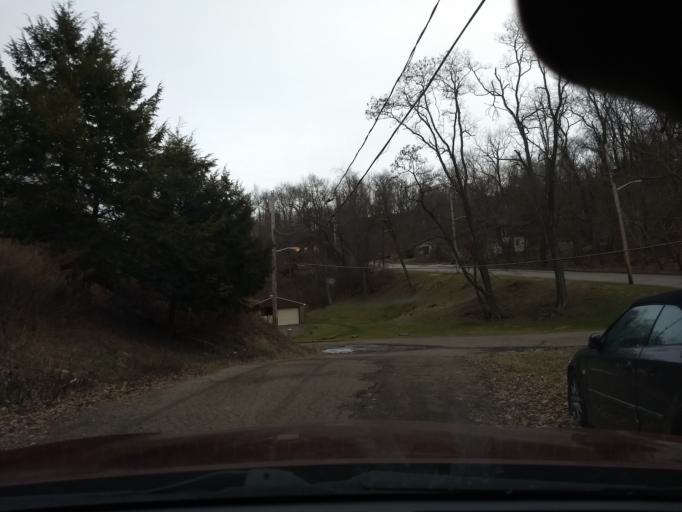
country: US
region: Pennsylvania
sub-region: Allegheny County
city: Homestead
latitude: 40.4133
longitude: -79.9340
